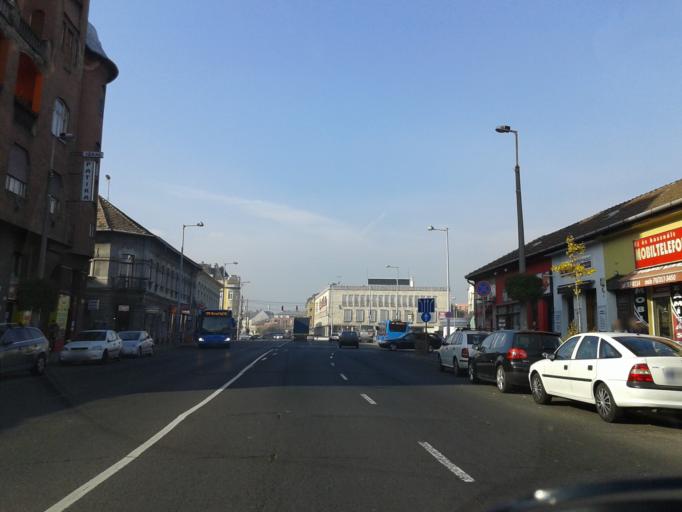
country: HU
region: Budapest
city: Budapest IV. keruelet
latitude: 47.5602
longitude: 19.0917
